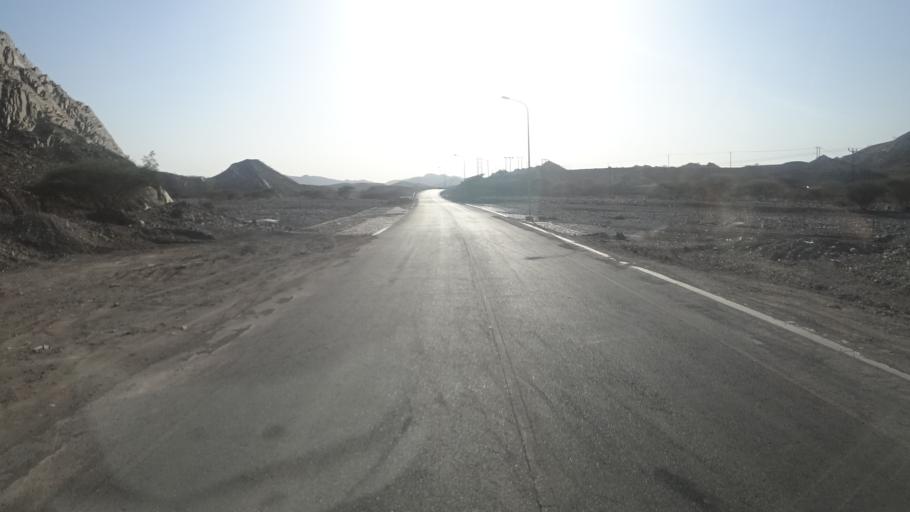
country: OM
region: Ash Sharqiyah
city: Badiyah
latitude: 22.5623
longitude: 59.0302
